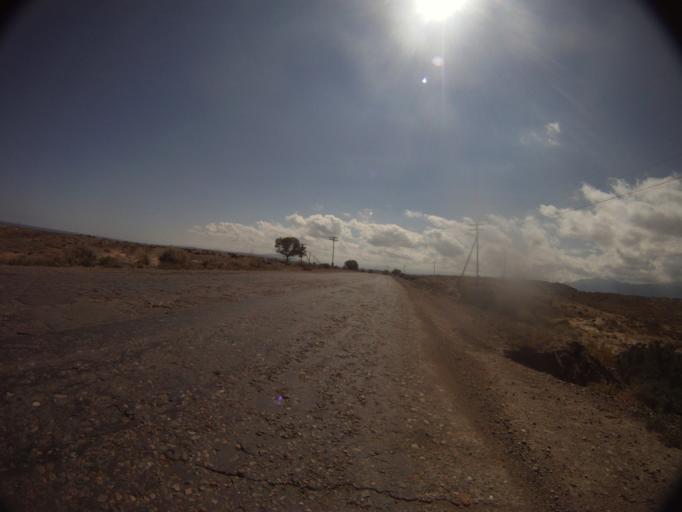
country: KG
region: Ysyk-Koel
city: Balykchy
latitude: 42.2849
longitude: 76.5202
